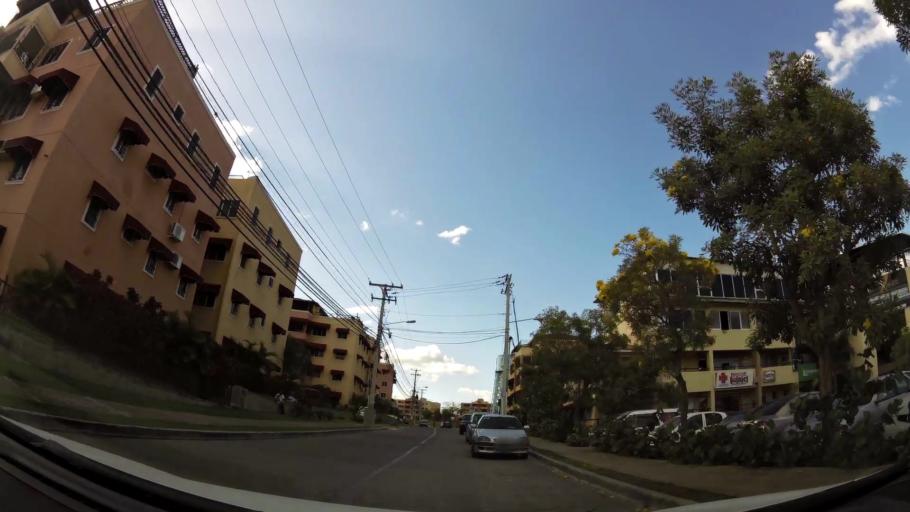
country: DO
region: Nacional
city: Santo Domingo
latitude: 18.5108
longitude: -69.9803
